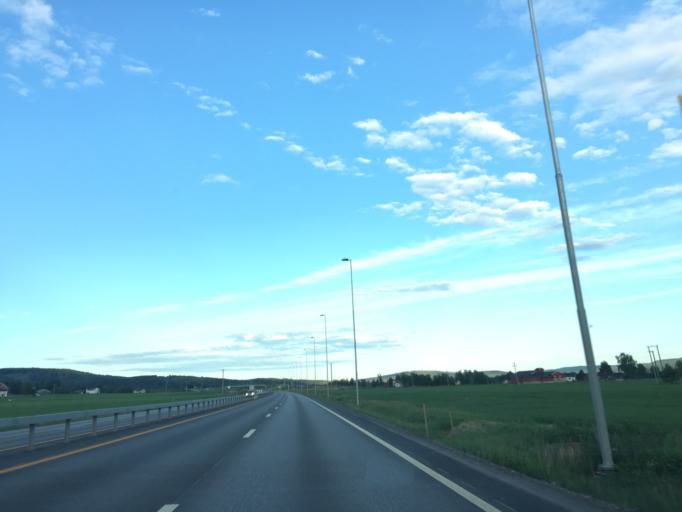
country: NO
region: Hedmark
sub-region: Kongsvinger
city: Spetalen
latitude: 60.2379
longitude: 11.8044
